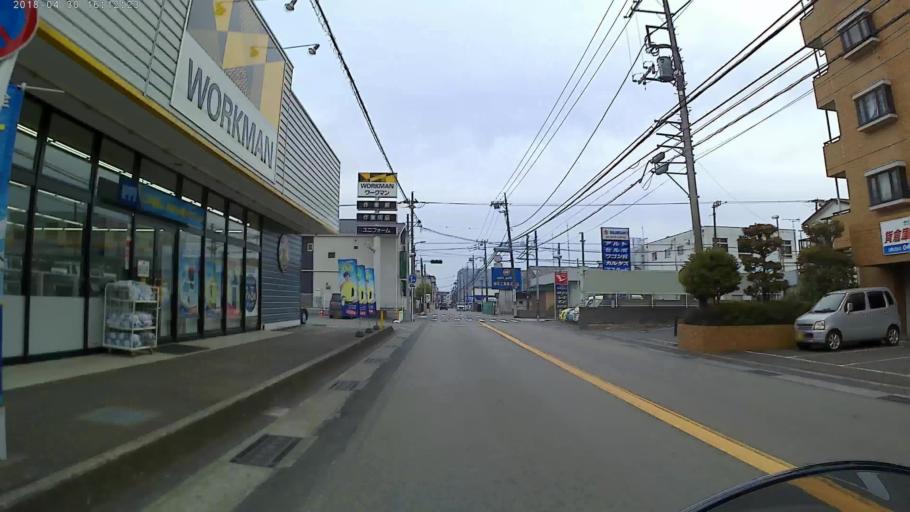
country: JP
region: Kanagawa
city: Minami-rinkan
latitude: 35.4965
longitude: 139.4291
